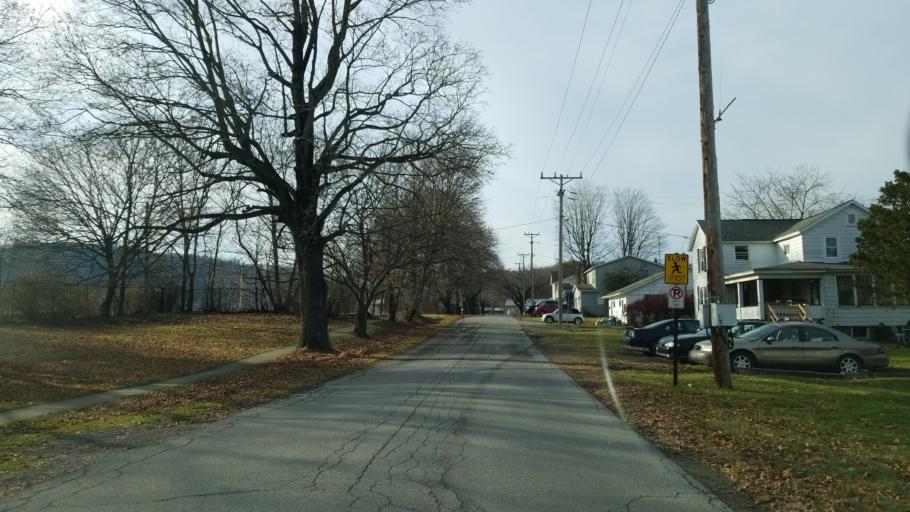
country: US
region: Pennsylvania
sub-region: Clearfield County
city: Clearfield
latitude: 41.0311
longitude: -78.4420
